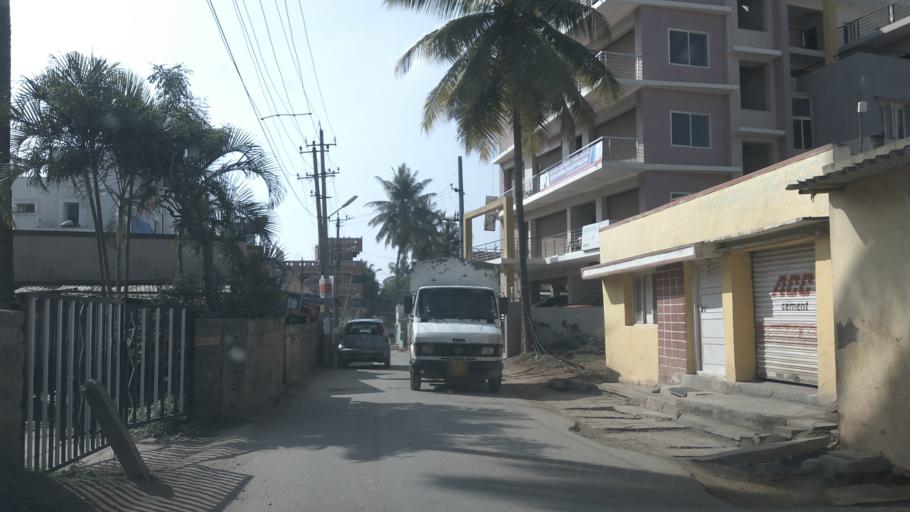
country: IN
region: Karnataka
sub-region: Bangalore Urban
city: Bangalore
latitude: 12.9468
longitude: 77.6813
